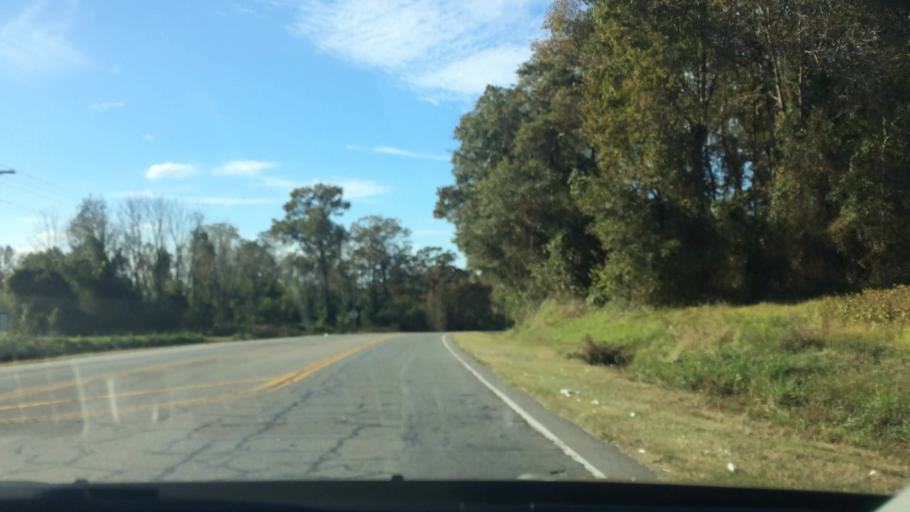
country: US
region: North Carolina
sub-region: Greene County
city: Snow Hill
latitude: 35.4564
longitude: -77.6950
